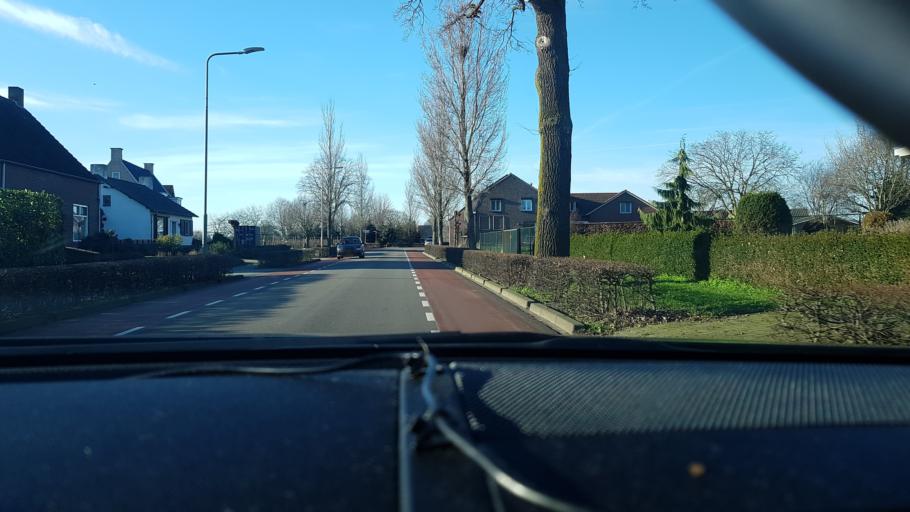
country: NL
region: Limburg
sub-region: Gemeente Peel en Maas
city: Maasbree
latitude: 51.3338
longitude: 5.9612
